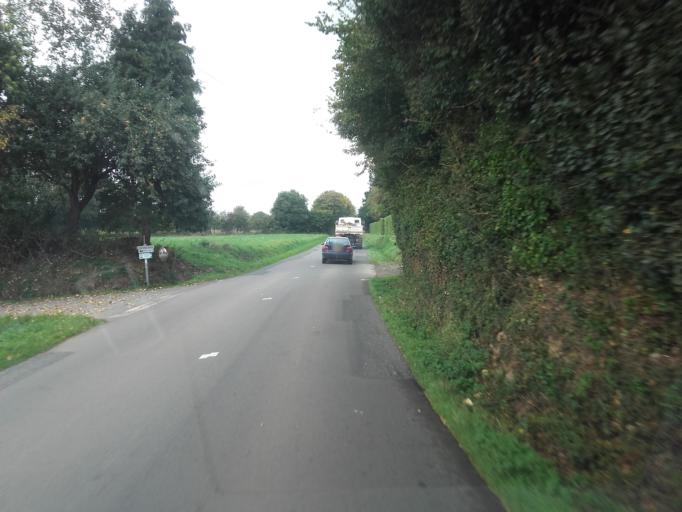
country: FR
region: Brittany
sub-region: Departement des Cotes-d'Armor
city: Plelo
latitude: 48.5755
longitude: -2.9504
